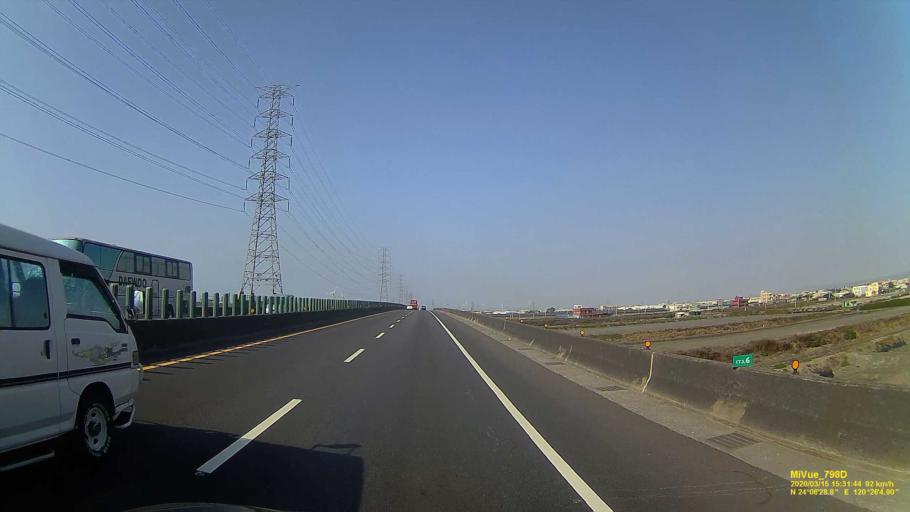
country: TW
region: Taiwan
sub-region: Changhua
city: Chang-hua
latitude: 24.1084
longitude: 120.4349
